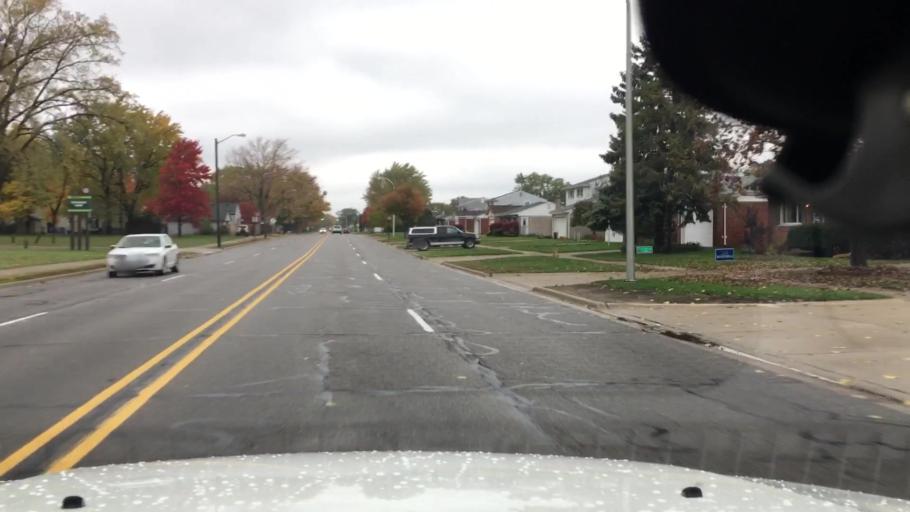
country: US
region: Michigan
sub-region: Oakland County
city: Clawson
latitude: 42.5243
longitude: -83.1258
